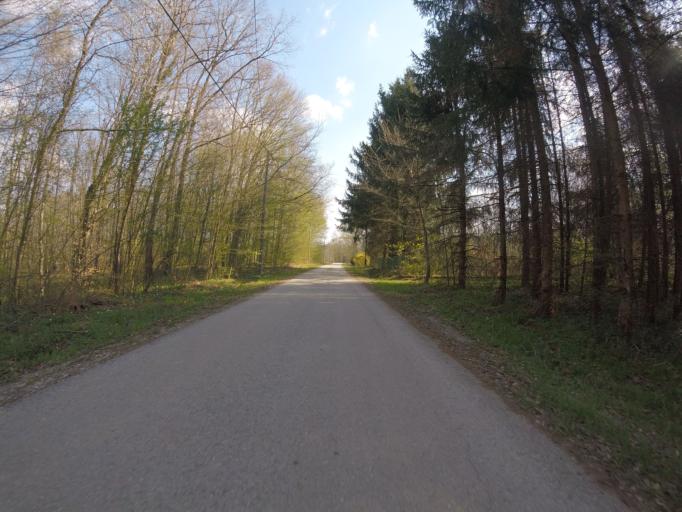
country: HR
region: Sisacko-Moslavacka
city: Glina
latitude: 45.4892
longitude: 16.0020
